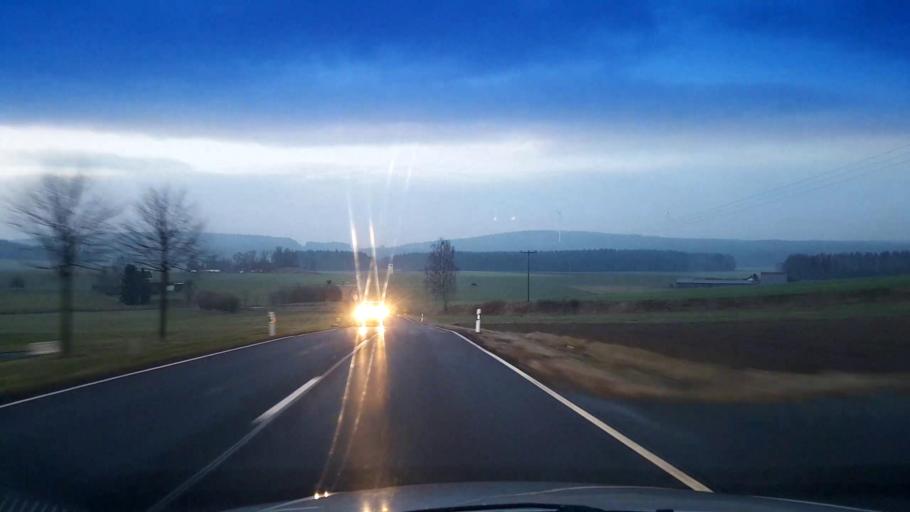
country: DE
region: Bavaria
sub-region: Upper Franconia
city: Arzberg
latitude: 50.0211
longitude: 12.2091
